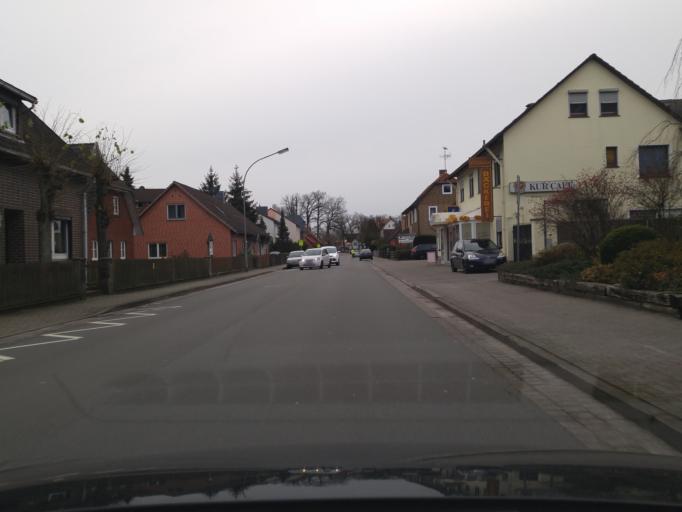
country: DE
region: Lower Saxony
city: Winsen (Aller)
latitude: 52.6858
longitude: 9.9104
